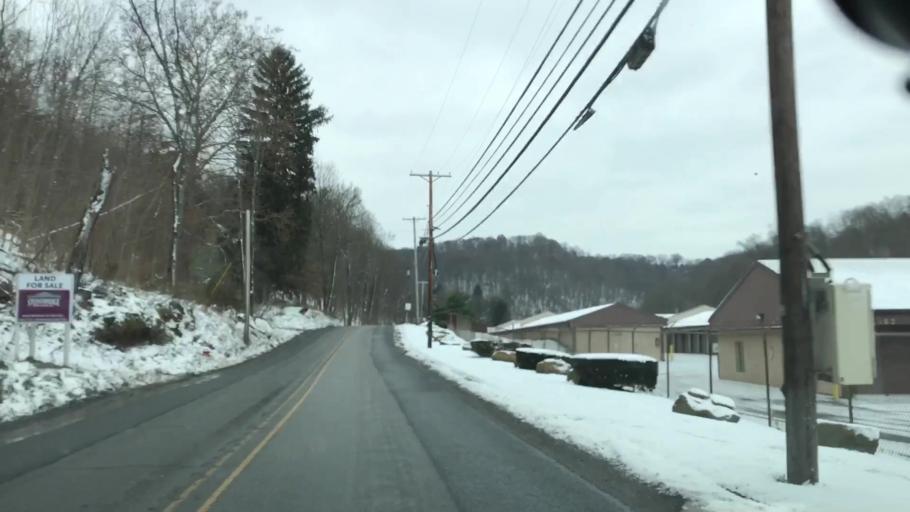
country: US
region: Pennsylvania
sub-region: Allegheny County
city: West View
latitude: 40.5339
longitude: -80.0579
